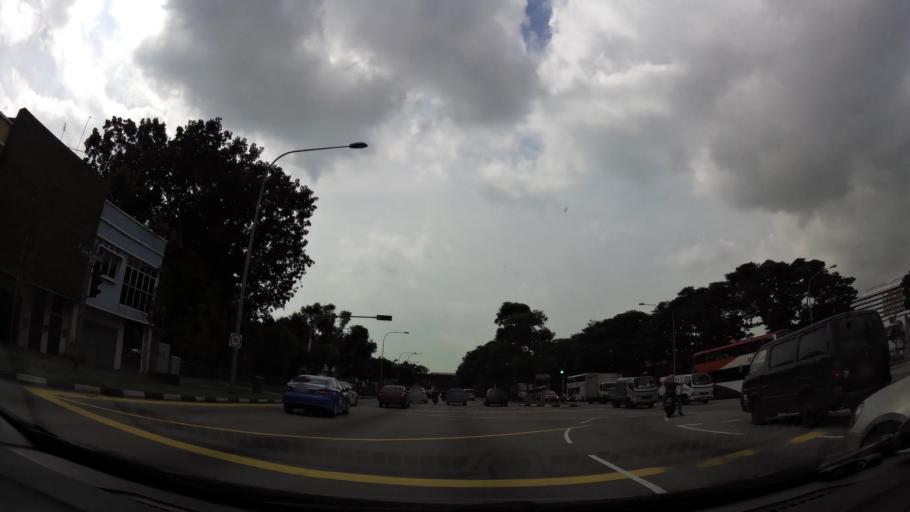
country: SG
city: Singapore
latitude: 1.3218
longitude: 103.9053
